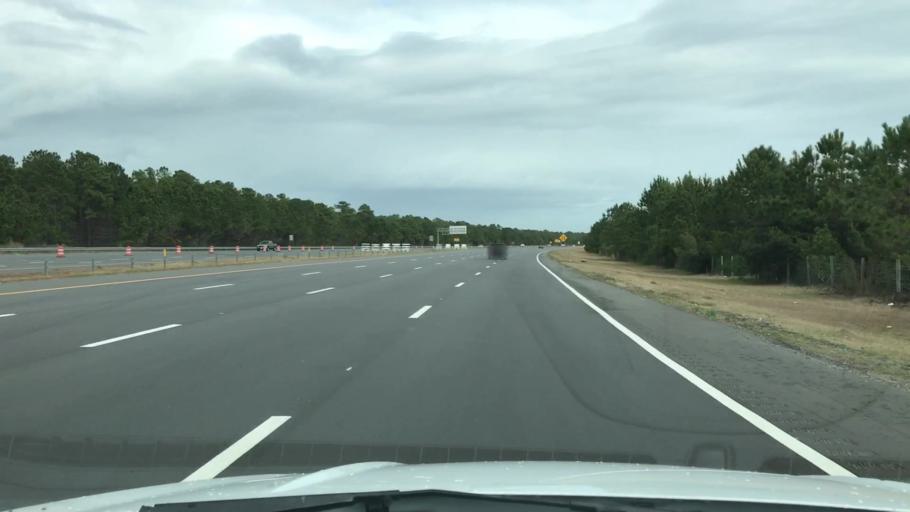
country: US
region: South Carolina
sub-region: Horry County
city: Socastee
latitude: 33.7072
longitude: -79.0106
